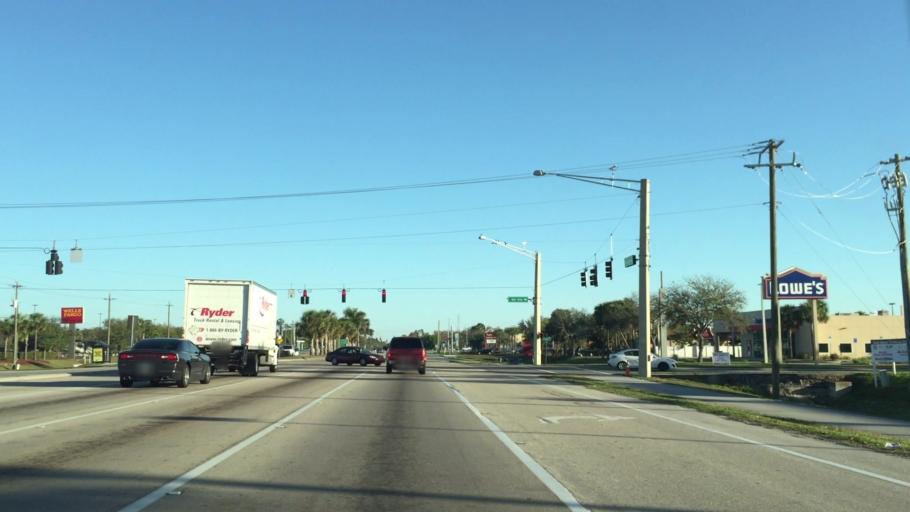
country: US
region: Florida
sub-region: Lee County
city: Fort Myers
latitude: 26.6085
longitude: -81.8111
